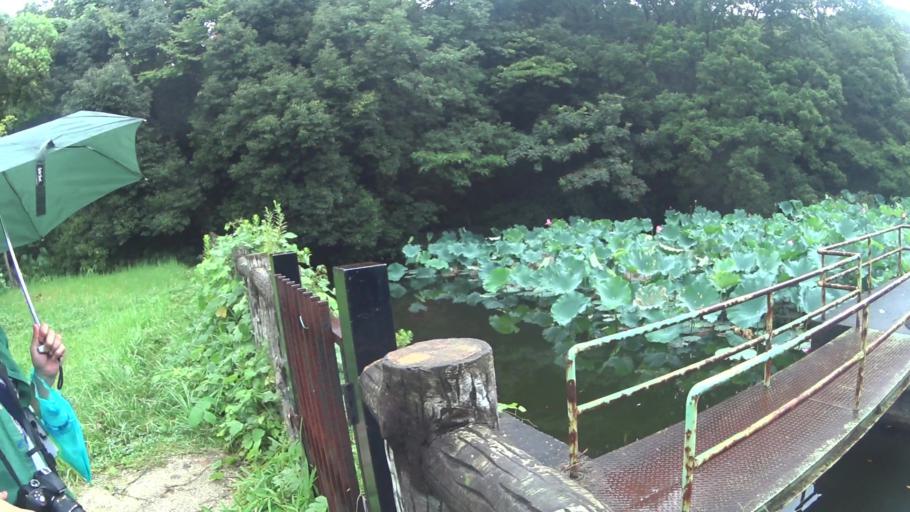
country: JP
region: Osaka
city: Takaishi
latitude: 34.5024
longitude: 135.4957
